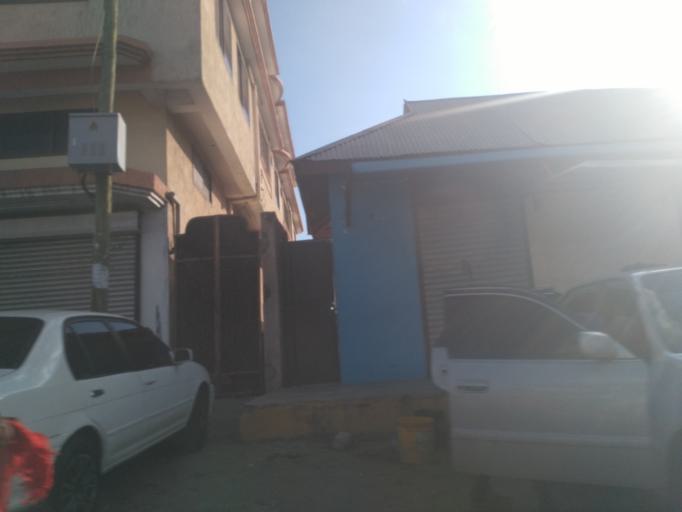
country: TZ
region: Dar es Salaam
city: Dar es Salaam
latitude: -6.8496
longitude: 39.2590
